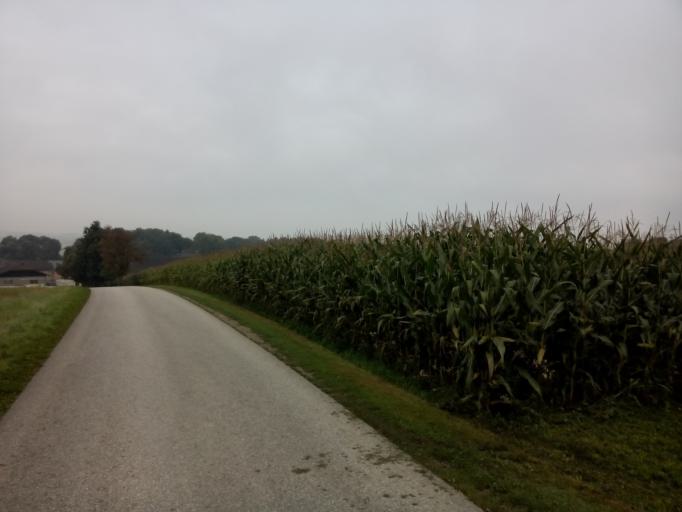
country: AT
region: Upper Austria
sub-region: Wels-Land
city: Sattledt
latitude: 48.0194
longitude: 14.0590
